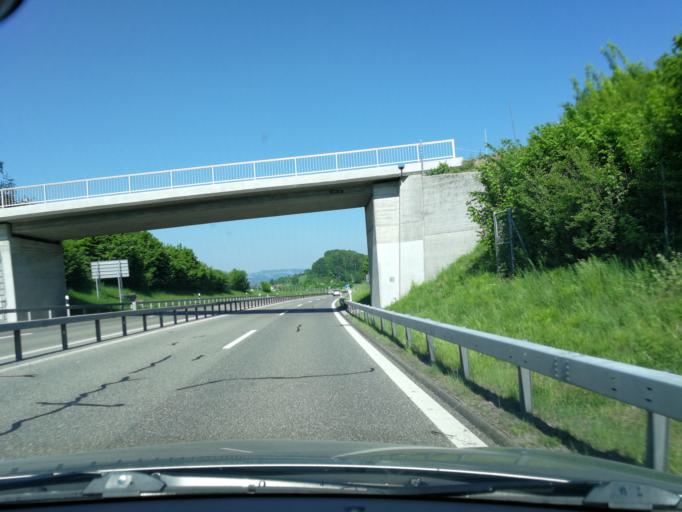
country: CH
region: Zurich
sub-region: Bezirk Hinwil
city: Gruet
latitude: 47.2899
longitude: 8.7932
